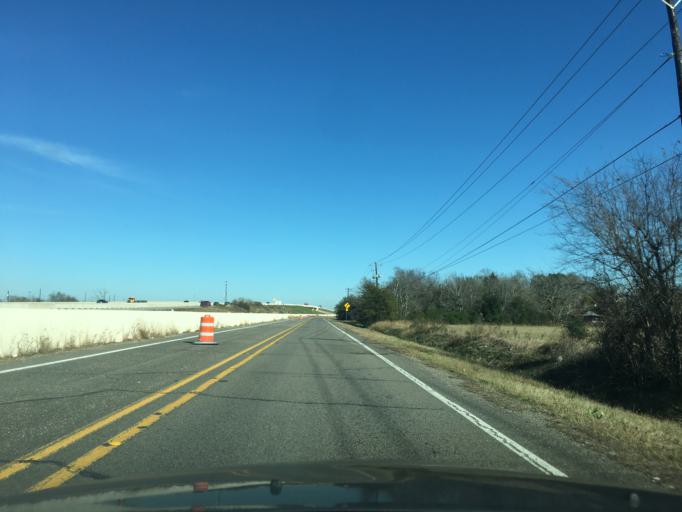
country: US
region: Texas
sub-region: Fort Bend County
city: Needville
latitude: 29.4817
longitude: -95.9418
